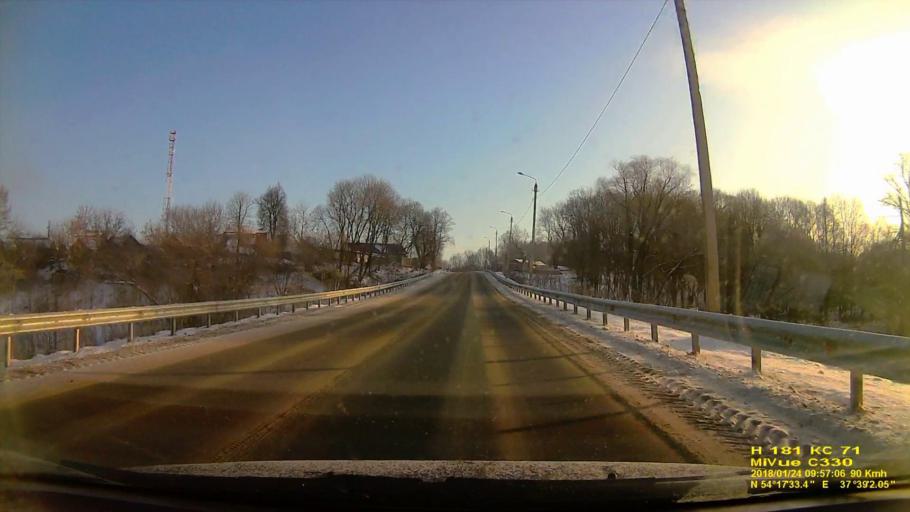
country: RU
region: Tula
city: Gorelki
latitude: 54.2927
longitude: 37.6508
